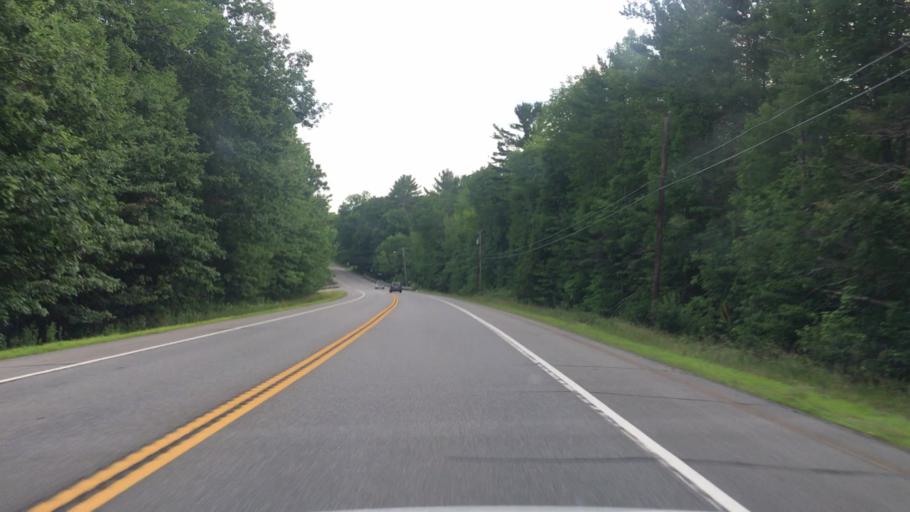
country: US
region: Maine
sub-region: Kennebec County
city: Windsor
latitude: 44.3577
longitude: -69.6429
